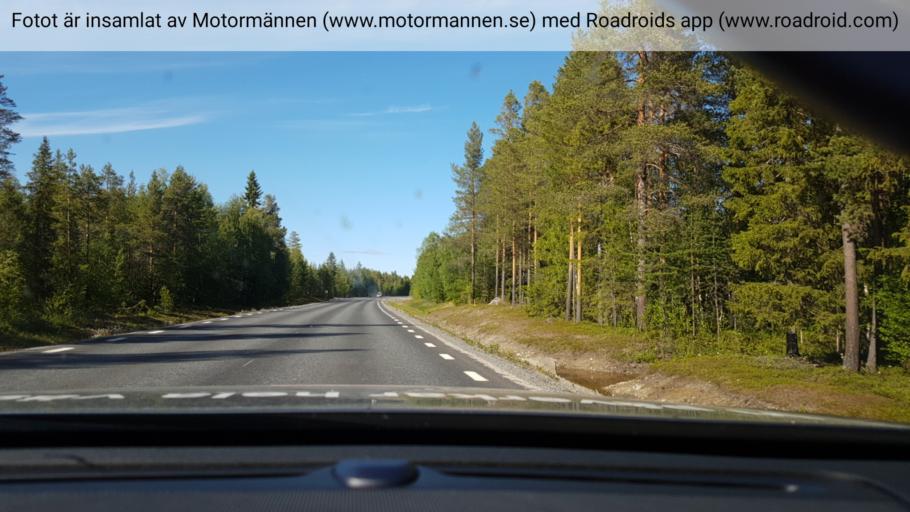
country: SE
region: Vaesterbotten
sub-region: Lycksele Kommun
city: Lycksele
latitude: 64.8038
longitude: 18.7325
